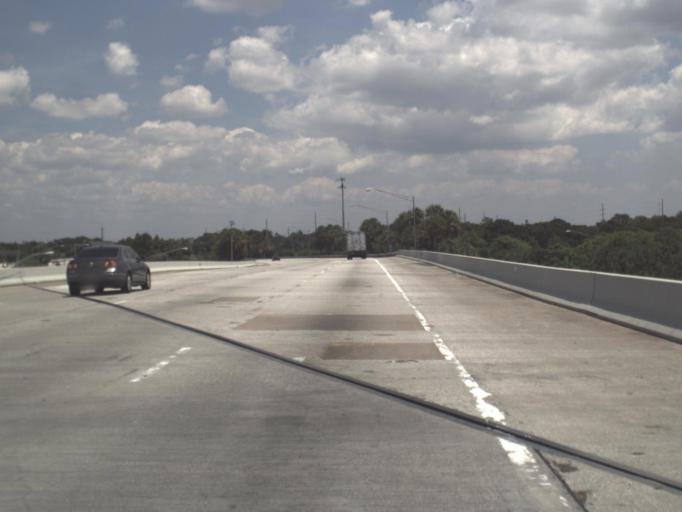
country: US
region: Florida
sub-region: Pinellas County
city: Gulfport
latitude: 27.7219
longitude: -82.6777
